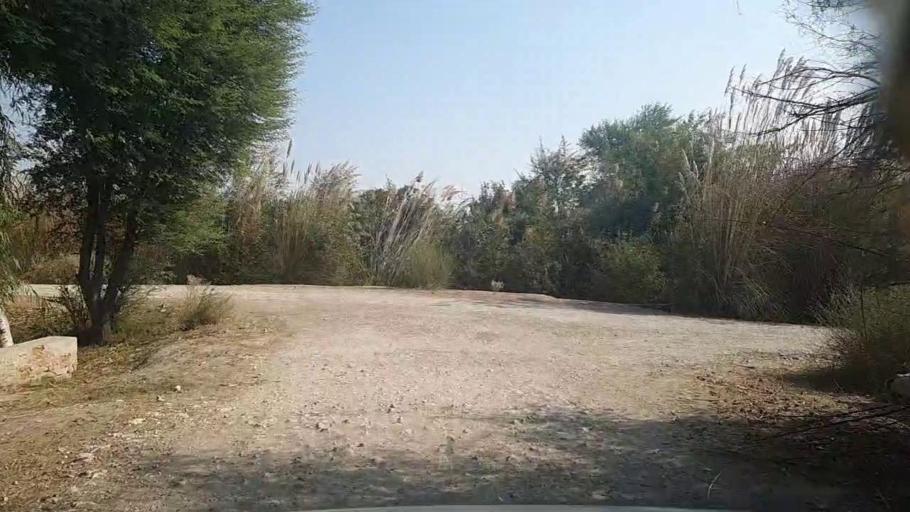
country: PK
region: Sindh
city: Kandiari
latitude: 26.9375
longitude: 68.5511
